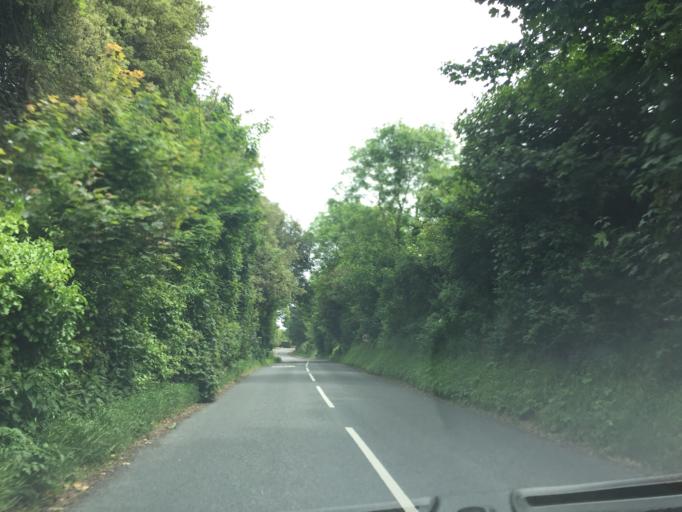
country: GB
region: England
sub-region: Dorset
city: Swanage
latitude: 50.6292
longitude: -1.9739
